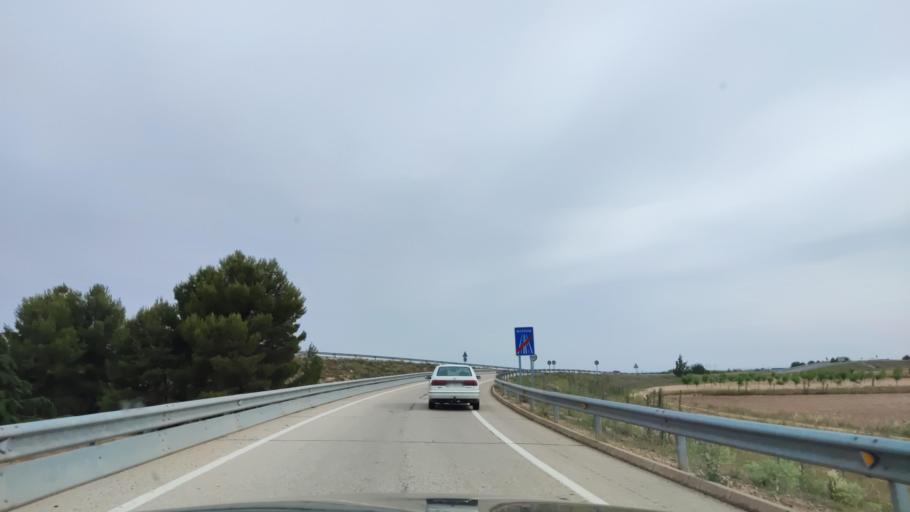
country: ES
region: Castille-La Mancha
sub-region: Provincia de Albacete
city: La Roda
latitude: 39.2256
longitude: -2.1893
